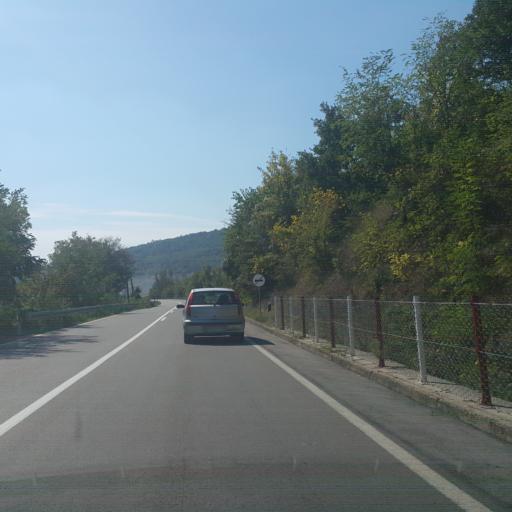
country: RS
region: Central Serbia
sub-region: Zajecarski Okrug
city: Zajecar
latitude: 43.8041
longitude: 22.3006
